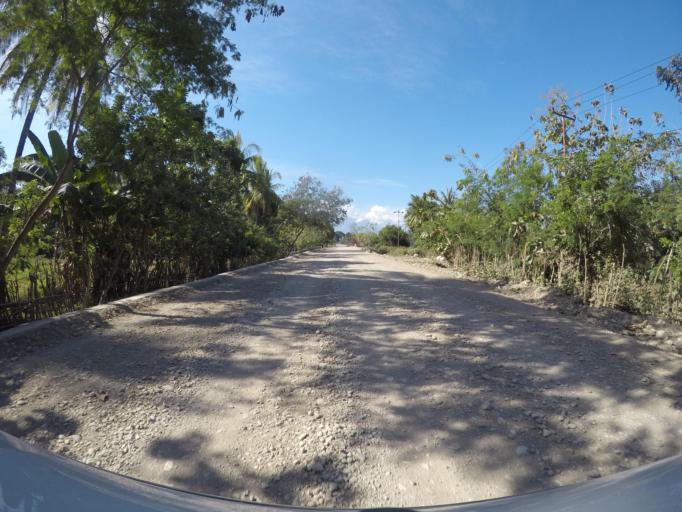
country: TL
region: Viqueque
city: Viqueque
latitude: -8.8552
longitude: 126.5111
